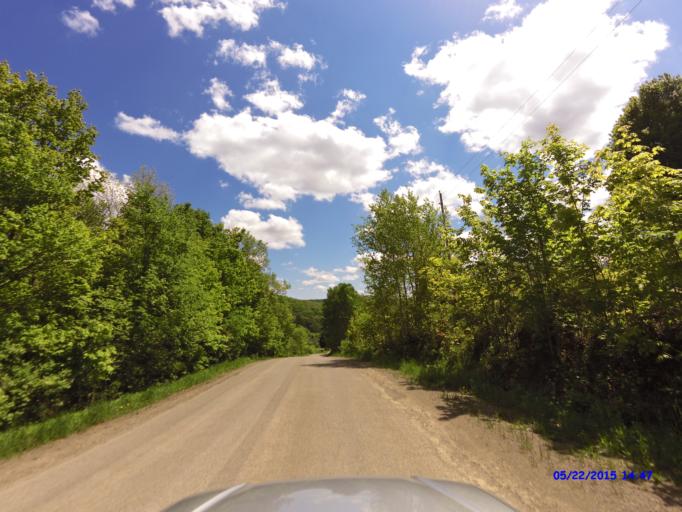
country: US
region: New York
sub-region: Cattaraugus County
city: Franklinville
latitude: 42.3484
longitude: -78.5844
